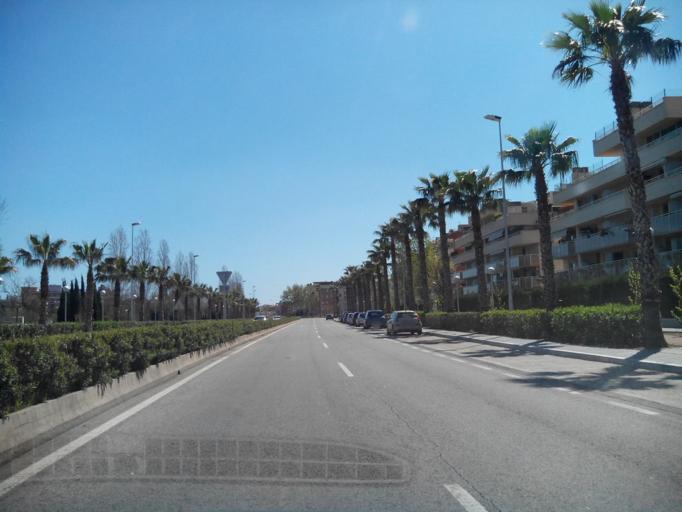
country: ES
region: Catalonia
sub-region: Provincia de Tarragona
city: Salou
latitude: 41.0833
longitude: 1.1375
